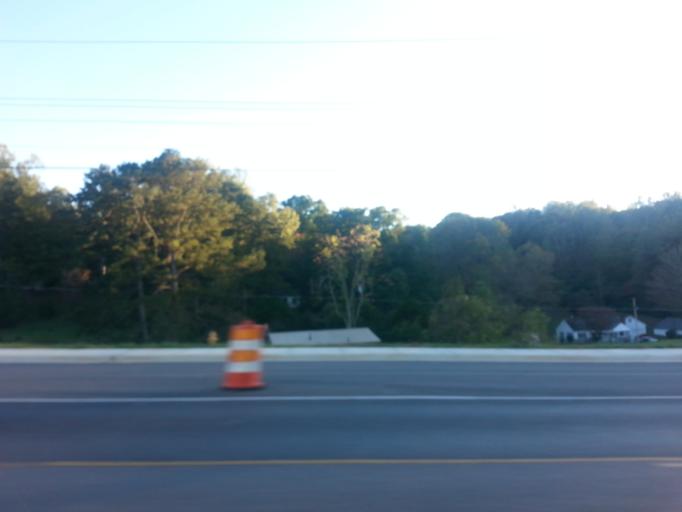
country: US
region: Tennessee
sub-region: Knox County
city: Knoxville
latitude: 35.9870
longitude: -84.0361
